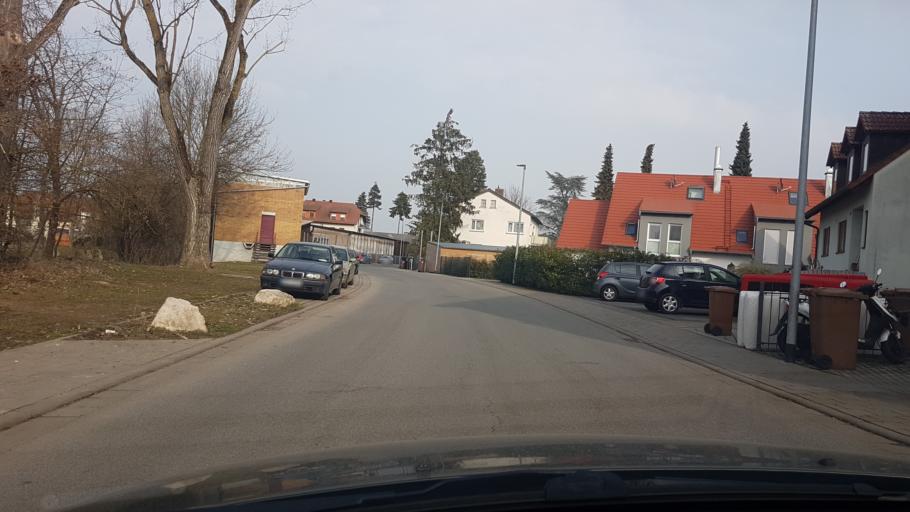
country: DE
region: Bavaria
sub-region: Upper Franconia
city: Hallstadt
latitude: 49.9266
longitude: 10.8667
